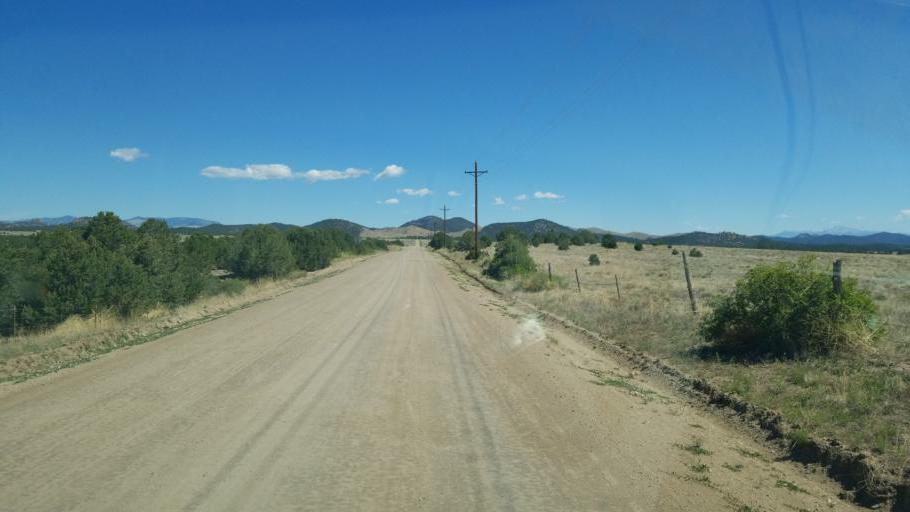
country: US
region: Colorado
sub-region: Custer County
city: Westcliffe
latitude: 38.2655
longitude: -105.5011
